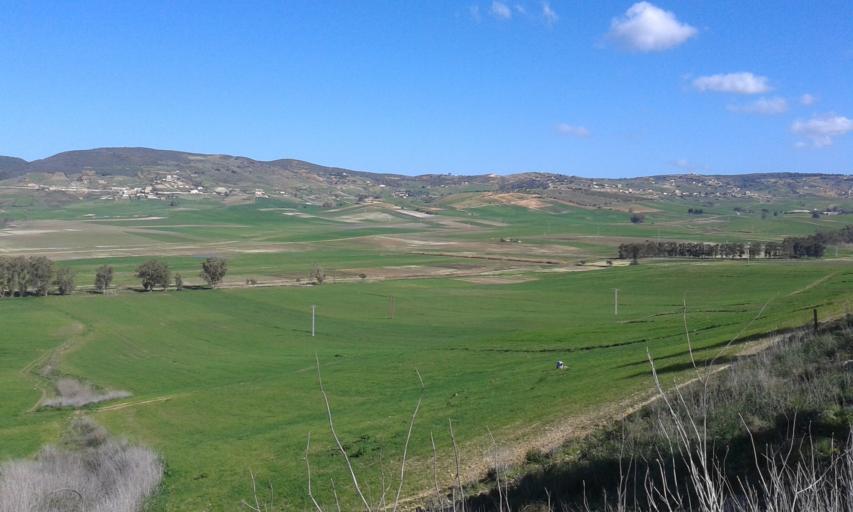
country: DZ
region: Relizane
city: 'Ain Merane
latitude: 36.2324
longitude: 0.8993
